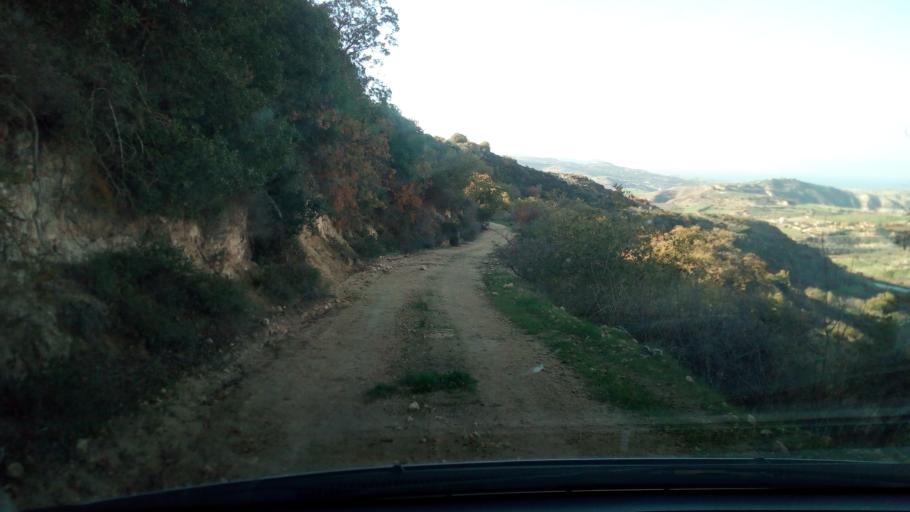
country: CY
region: Pafos
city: Polis
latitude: 34.9423
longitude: 32.4867
